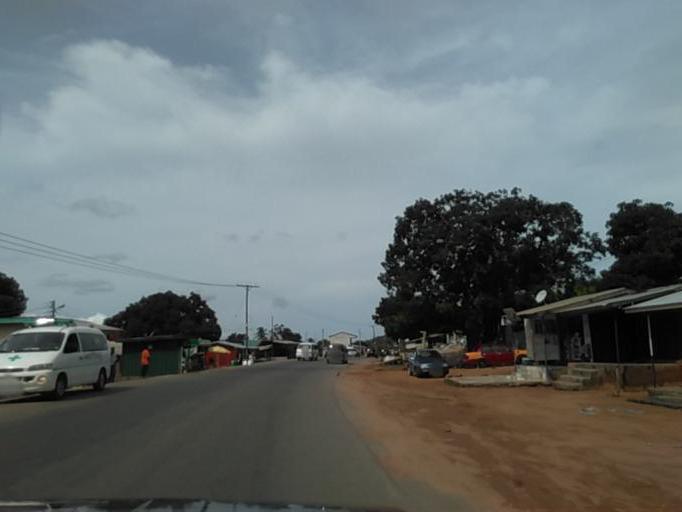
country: GH
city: Akropong
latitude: 6.2316
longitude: 0.0918
